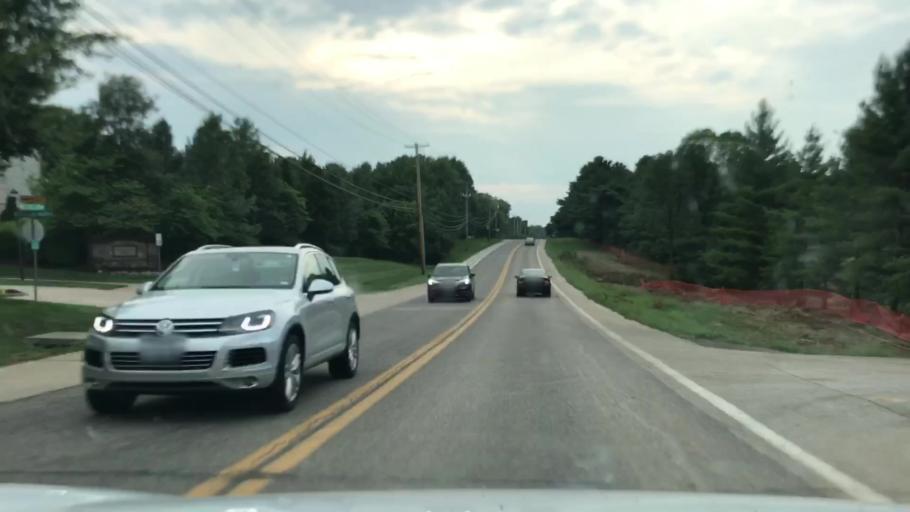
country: US
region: Missouri
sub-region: Saint Louis County
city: Chesterfield
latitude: 38.6549
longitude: -90.6044
